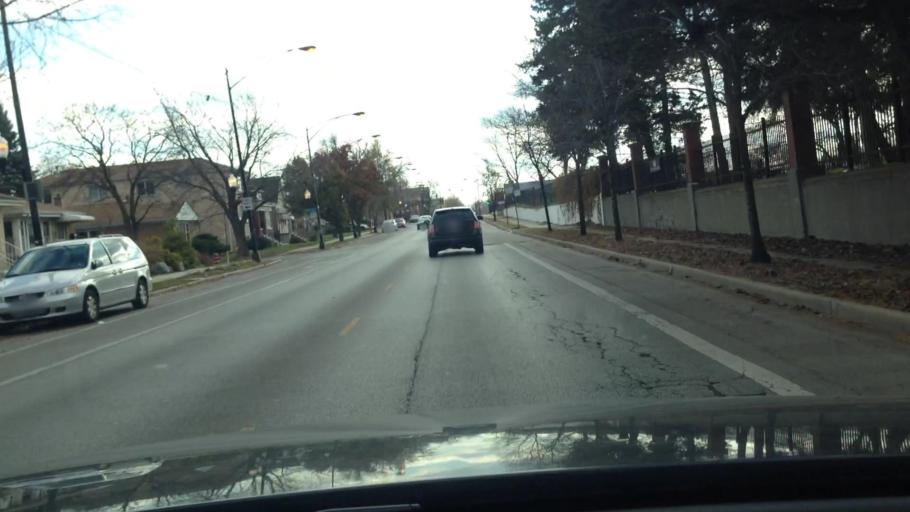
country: US
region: Illinois
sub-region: Cook County
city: Harwood Heights
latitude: 41.9480
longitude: -87.7863
